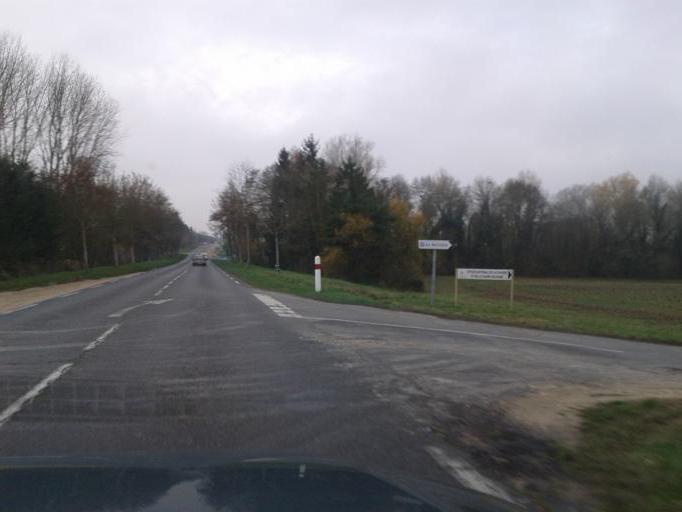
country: FR
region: Centre
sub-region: Departement du Loiret
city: Lailly-en-Val
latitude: 47.7793
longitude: 1.7023
